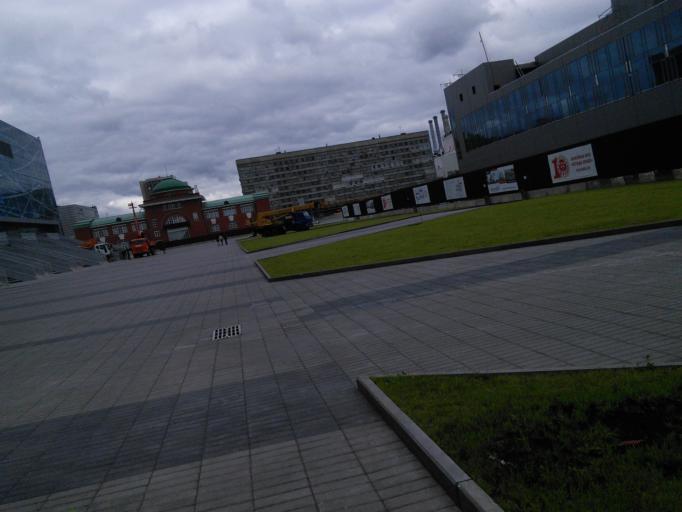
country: RU
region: Moskovskaya
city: Kozhukhovo
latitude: 55.7010
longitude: 37.6462
